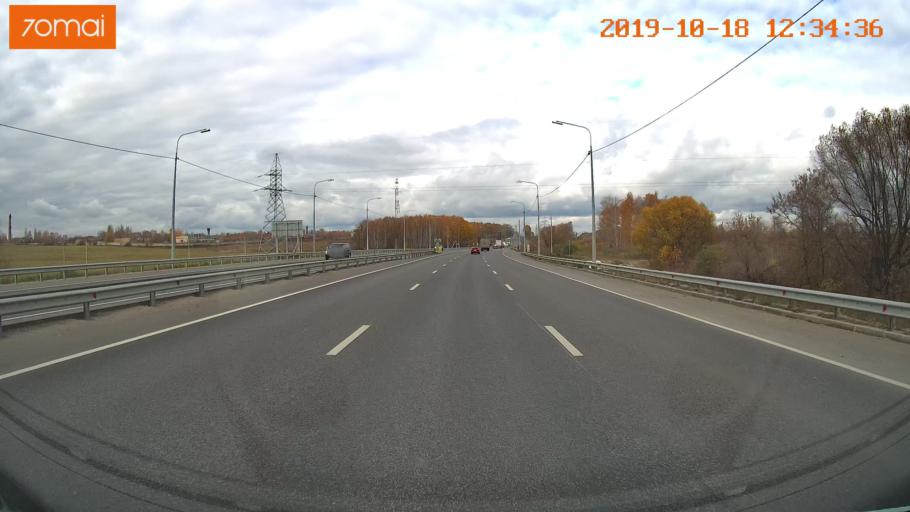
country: RU
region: Rjazan
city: Ryazan'
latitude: 54.6158
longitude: 39.6375
